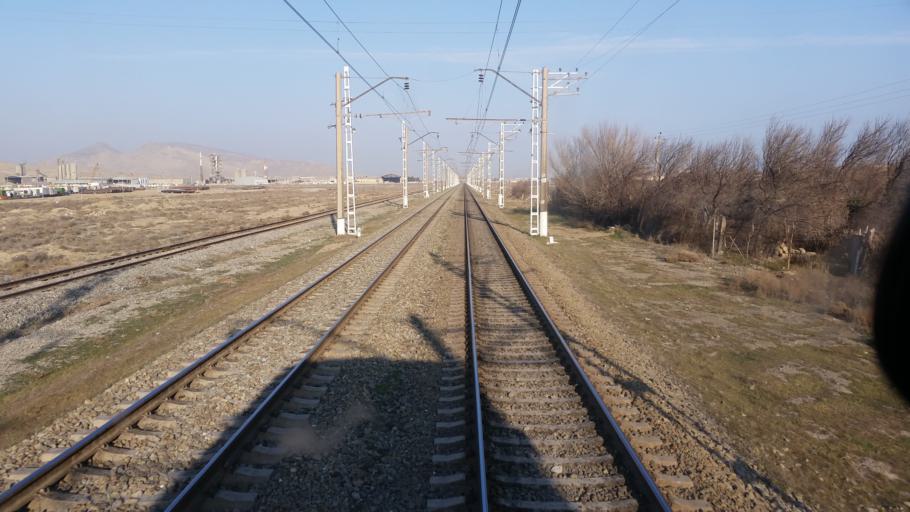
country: AZ
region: Baki
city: Korgoz
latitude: 40.2317
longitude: 49.5769
